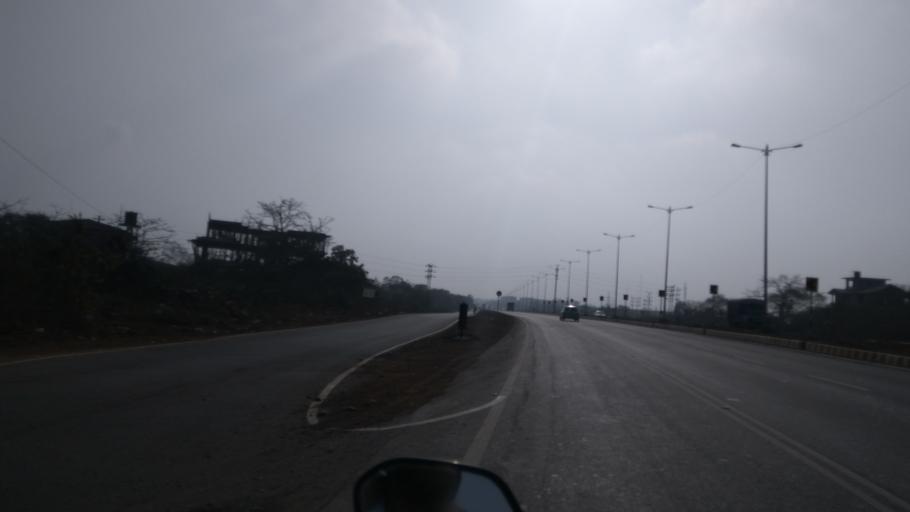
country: IN
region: Goa
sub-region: North Goa
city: Bambolim
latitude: 15.4938
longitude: 73.8828
